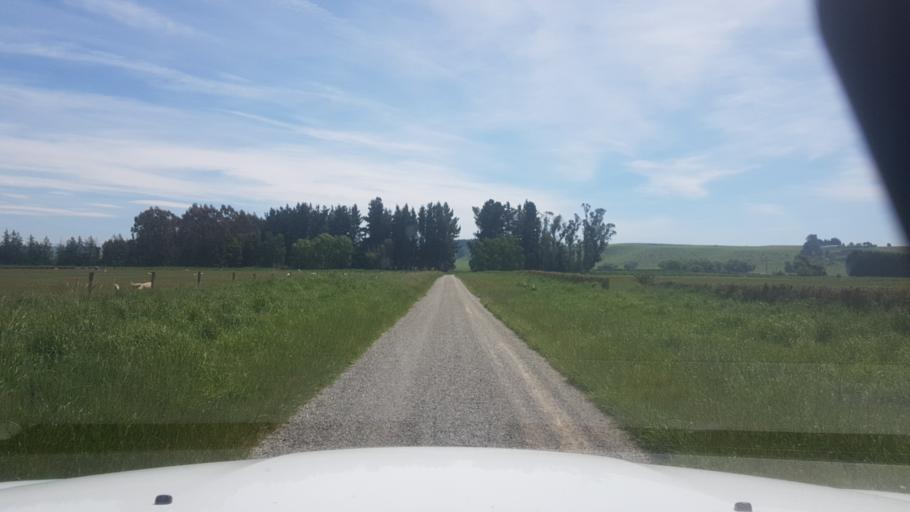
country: NZ
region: Canterbury
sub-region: Timaru District
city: Pleasant Point
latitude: -44.2229
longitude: 171.1635
